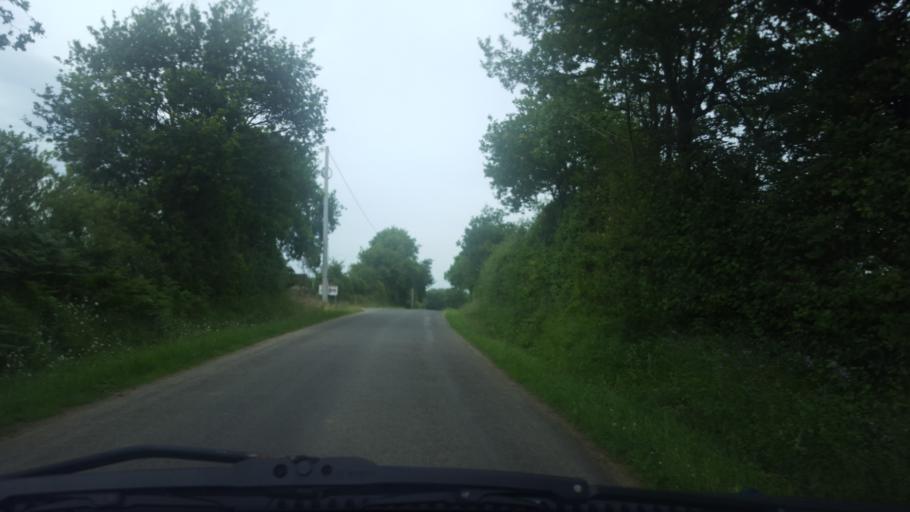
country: FR
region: Pays de la Loire
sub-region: Departement de la Loire-Atlantique
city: La Limouziniere
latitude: 46.9971
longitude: -1.5864
